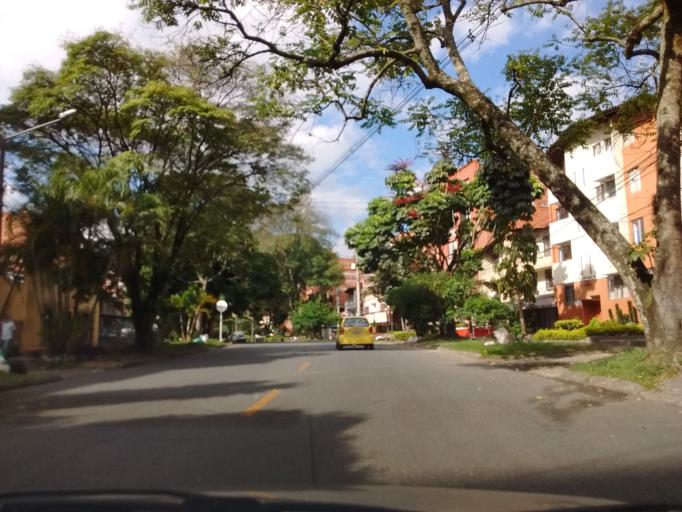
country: CO
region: Antioquia
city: Medellin
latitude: 6.2436
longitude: -75.6074
